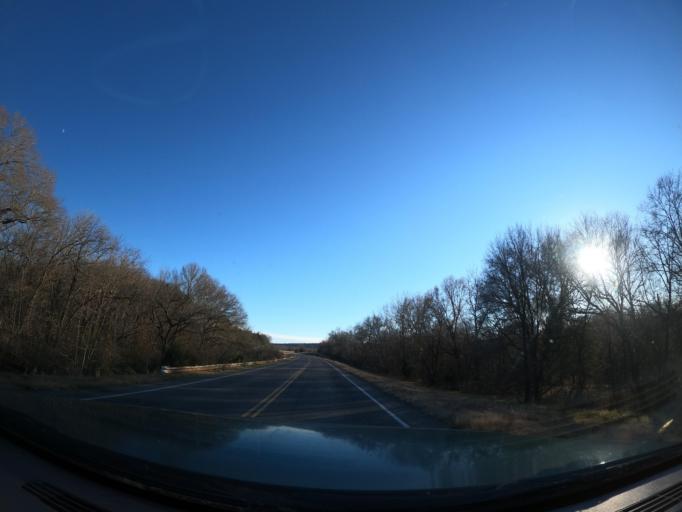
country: US
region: Oklahoma
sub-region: Latimer County
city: Wilburton
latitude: 34.9388
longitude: -95.3412
